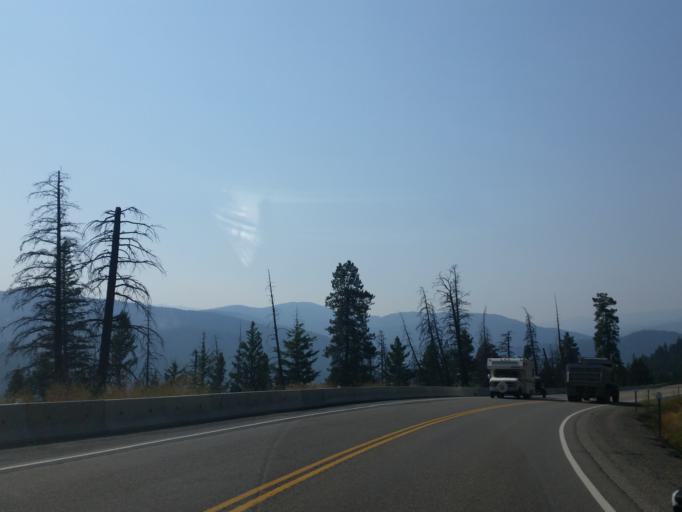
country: CA
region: British Columbia
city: Princeton
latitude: 49.2197
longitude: -120.5474
